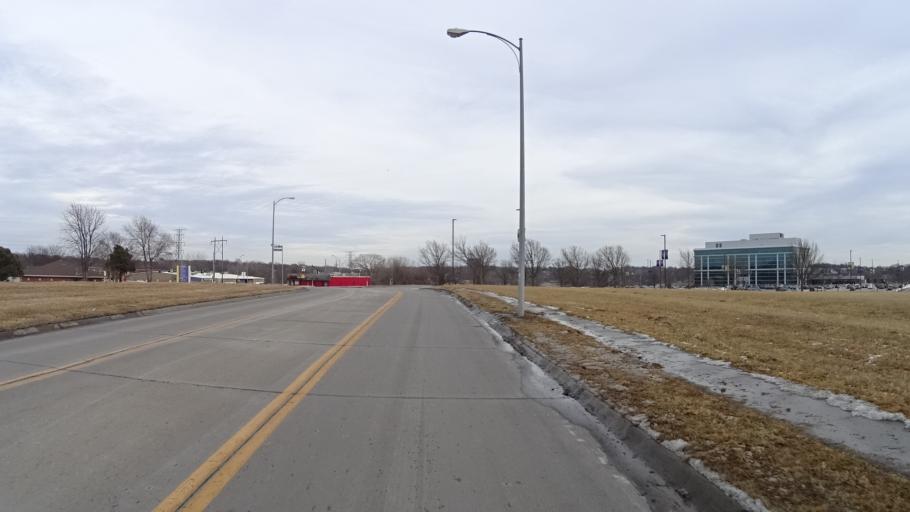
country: US
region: Nebraska
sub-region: Sarpy County
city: Offutt Air Force Base
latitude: 41.1535
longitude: -95.9242
